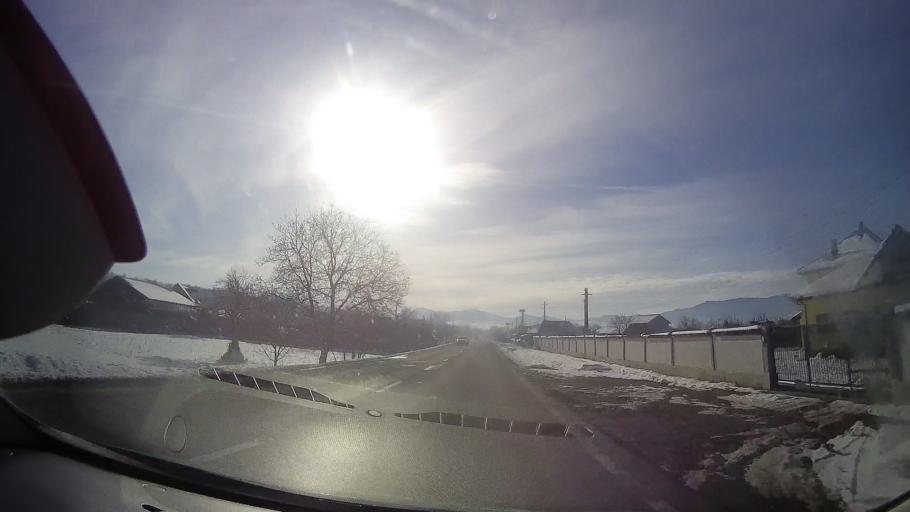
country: RO
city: Vanatori-Neamt
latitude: 47.1694
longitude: 26.3220
